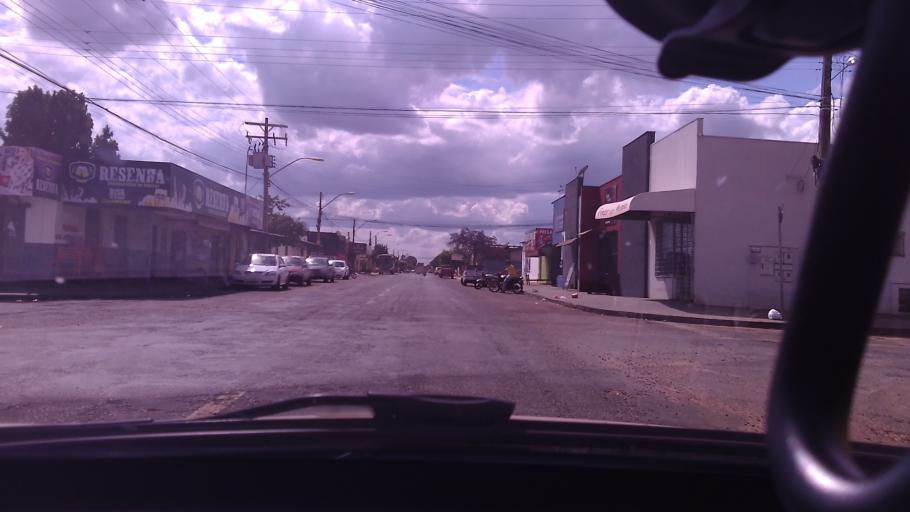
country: BR
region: Goias
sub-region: Mineiros
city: Mineiros
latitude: -17.5431
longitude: -52.5440
